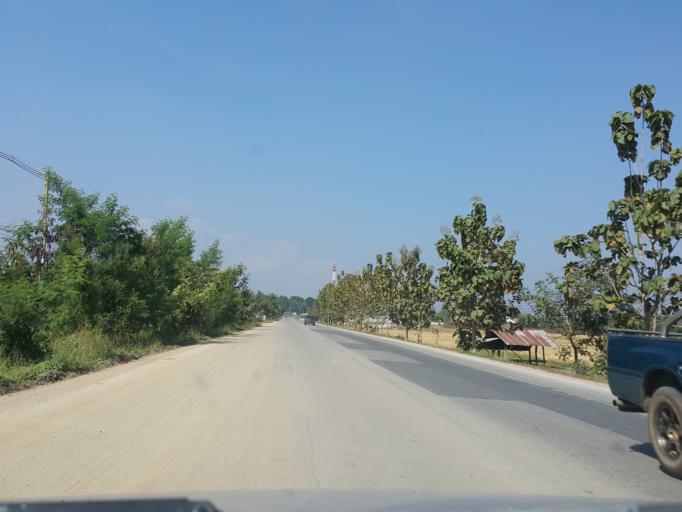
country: TH
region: Chiang Mai
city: San Sai
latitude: 18.8625
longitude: 98.9904
